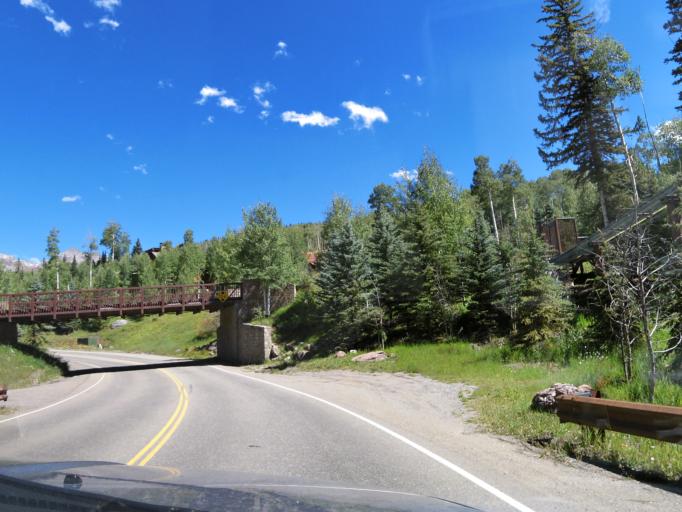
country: US
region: Colorado
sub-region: San Miguel County
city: Mountain Village
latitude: 37.9329
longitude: -107.8498
